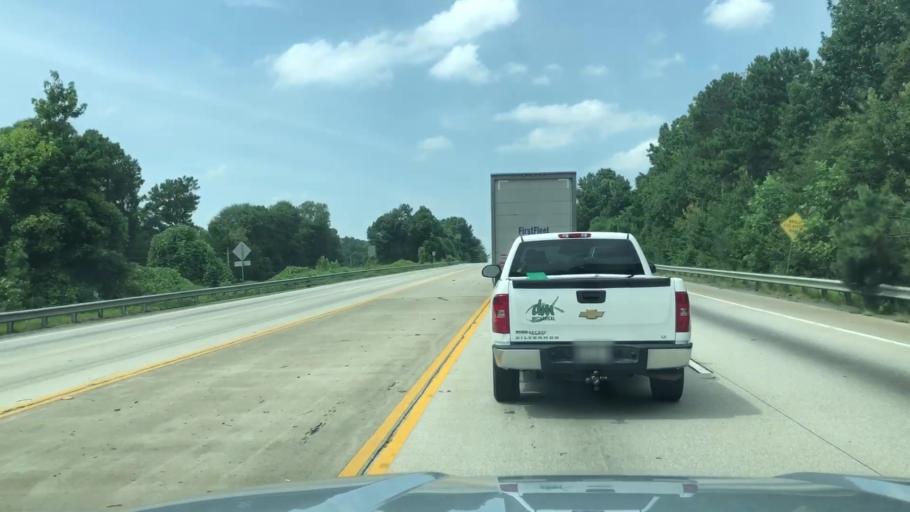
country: US
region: Georgia
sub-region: Douglas County
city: Lithia Springs
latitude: 33.8037
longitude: -84.6517
